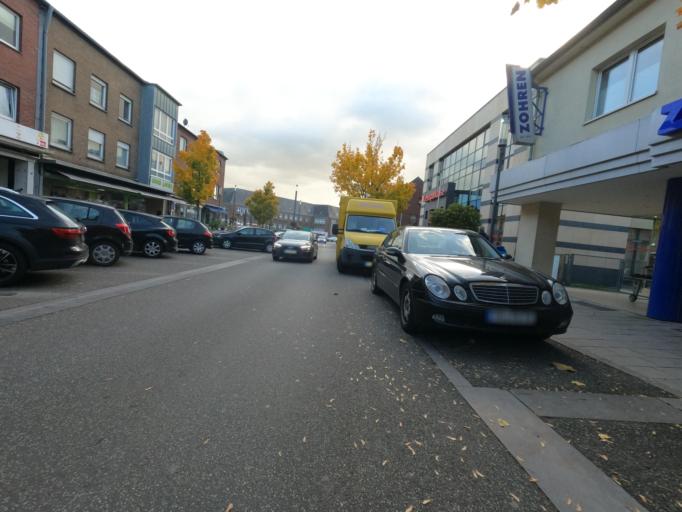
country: DE
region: North Rhine-Westphalia
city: Huckelhoven
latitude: 51.0558
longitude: 6.2226
